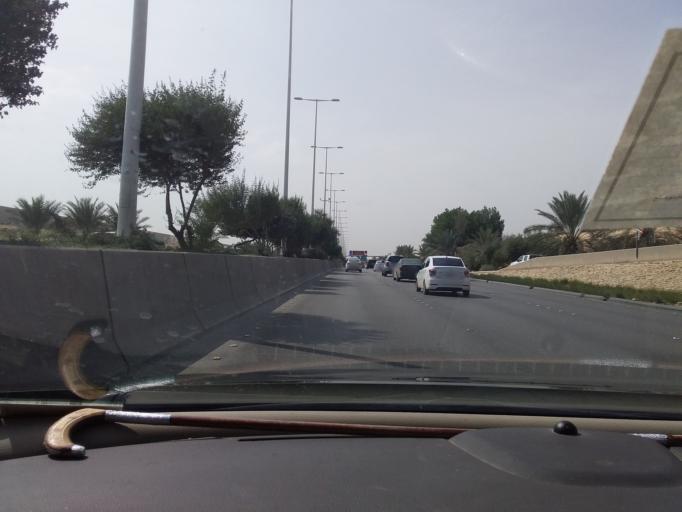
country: SA
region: Ar Riyad
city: Riyadh
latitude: 24.7310
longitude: 46.7240
